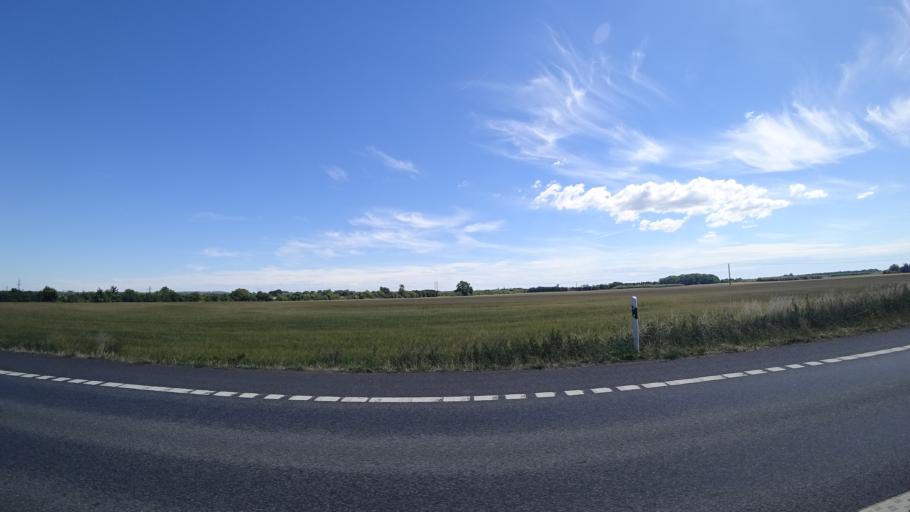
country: SE
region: Skane
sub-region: Kristianstads Kommun
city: Kristianstad
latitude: 56.0371
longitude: 14.0950
